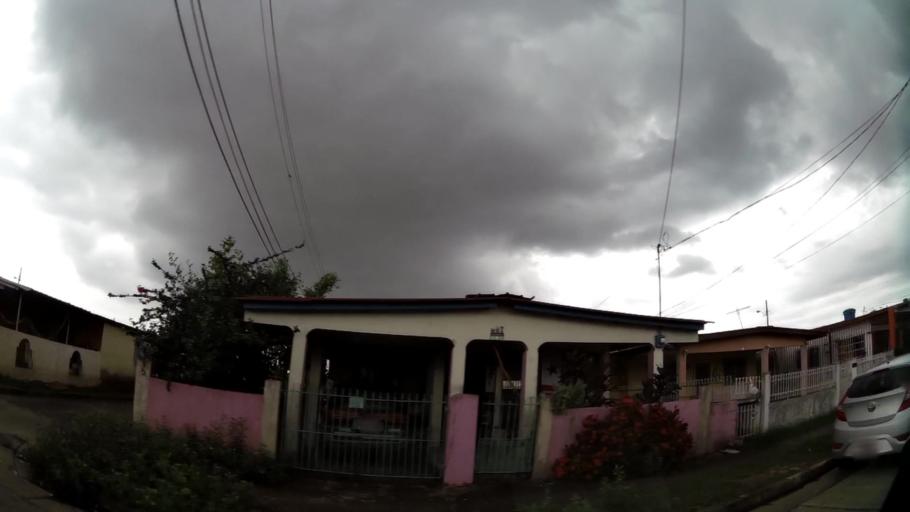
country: PA
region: Panama
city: Tocumen
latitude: 9.0589
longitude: -79.4175
